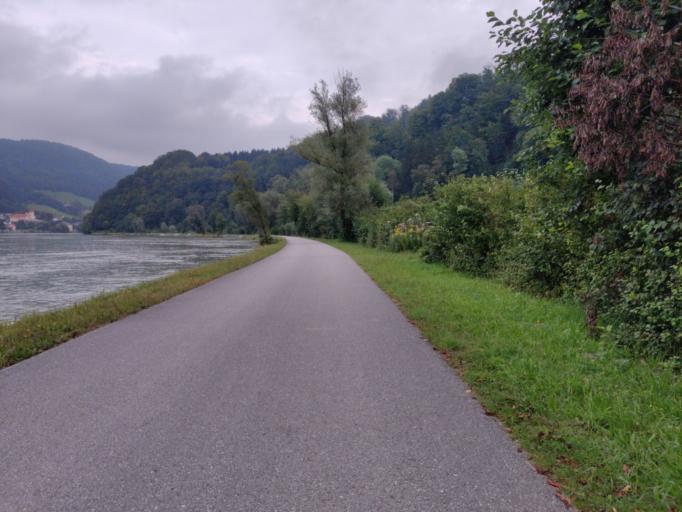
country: AT
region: Lower Austria
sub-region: Politischer Bezirk Melk
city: Nochling
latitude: 48.2269
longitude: 14.8954
